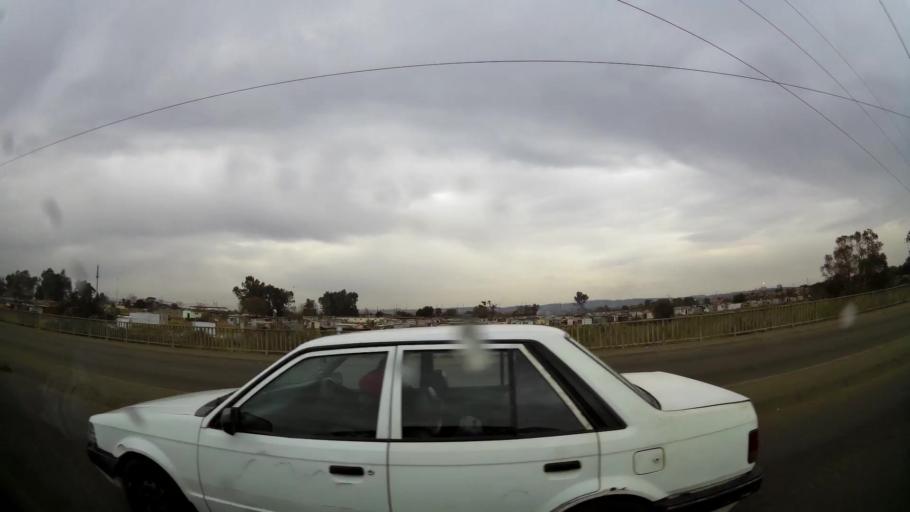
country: ZA
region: Gauteng
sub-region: City of Tshwane Metropolitan Municipality
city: Pretoria
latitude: -25.7184
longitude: 28.3564
